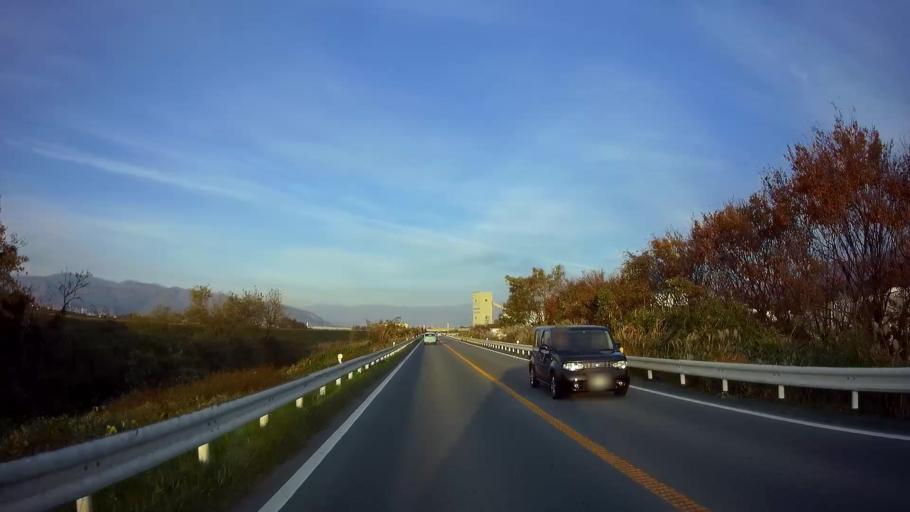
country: JP
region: Yamanashi
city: Kofu-shi
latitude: 35.5940
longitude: 138.5647
